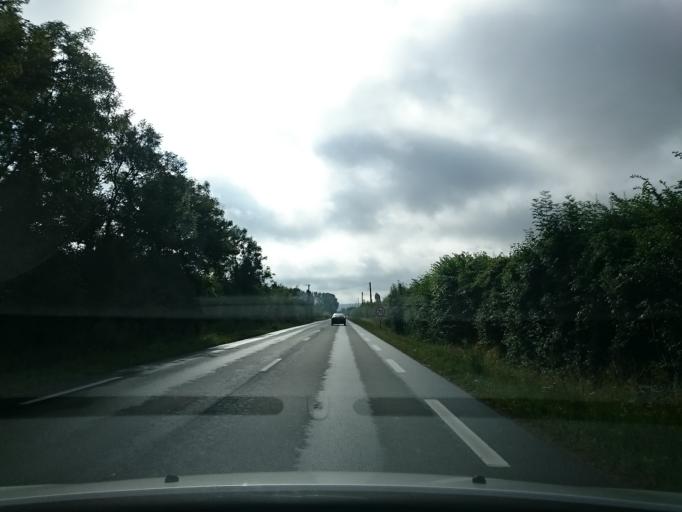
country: FR
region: Lower Normandy
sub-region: Departement du Calvados
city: Cambremer
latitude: 49.1161
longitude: 0.0309
